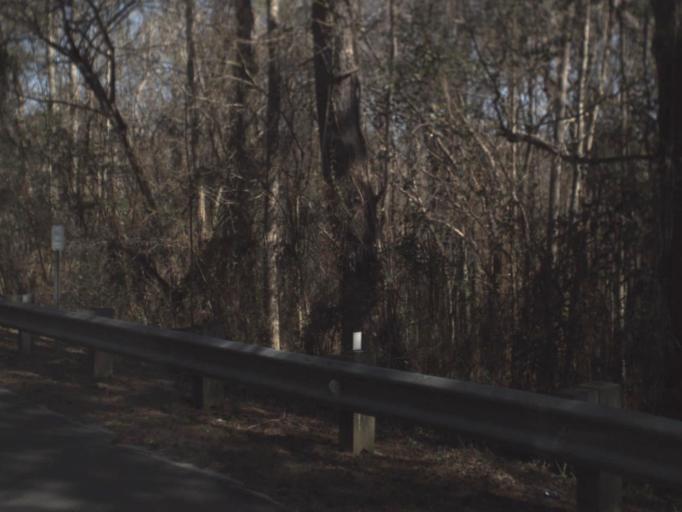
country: US
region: Florida
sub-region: Gulf County
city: Wewahitchka
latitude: 30.2860
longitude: -85.1460
